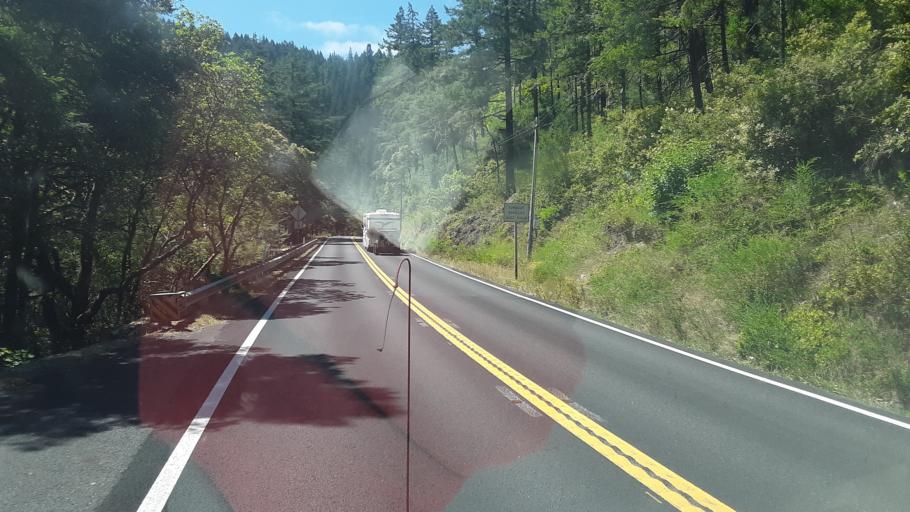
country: US
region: California
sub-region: Del Norte County
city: Bertsch-Oceanview
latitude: 41.8122
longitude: -124.0447
